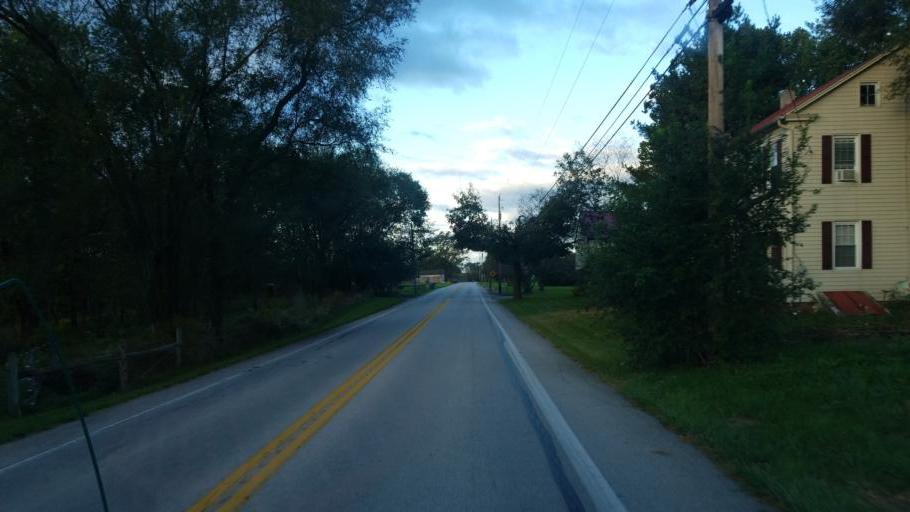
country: US
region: Pennsylvania
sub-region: Adams County
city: East Berlin
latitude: 39.9373
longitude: -76.9135
